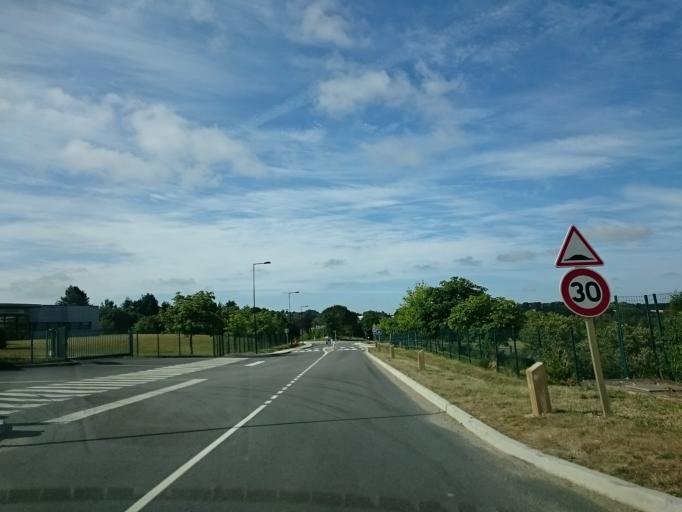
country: FR
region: Brittany
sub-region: Departement d'Ille-et-Vilaine
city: Crevin
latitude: 47.9389
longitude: -1.6685
